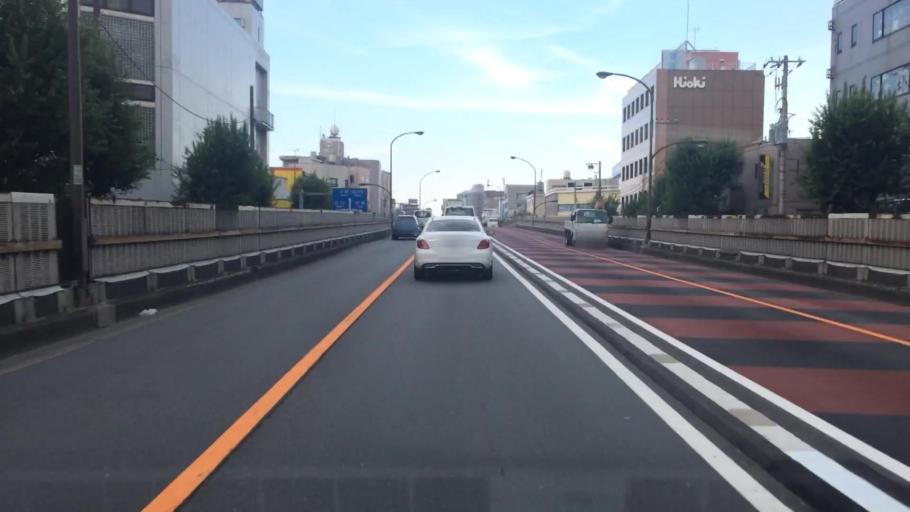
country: JP
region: Tokyo
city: Tokyo
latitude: 35.7241
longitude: 139.6538
